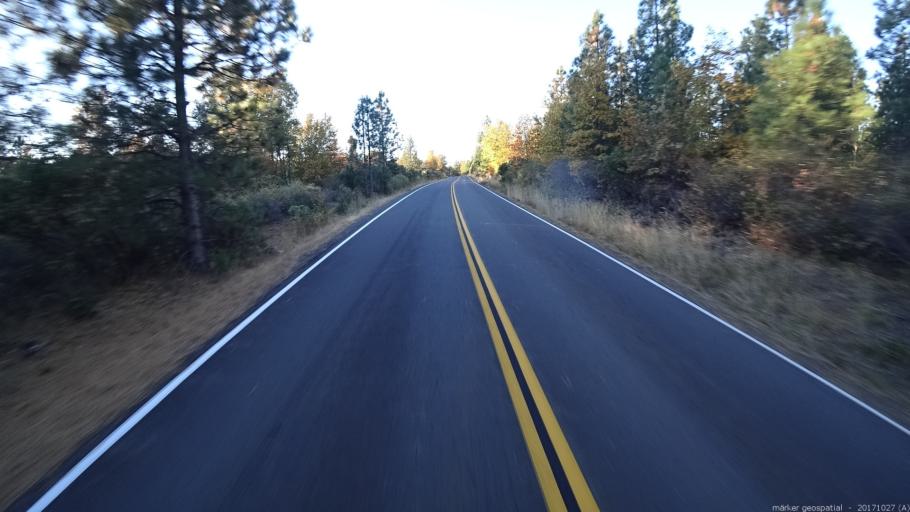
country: US
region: California
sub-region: Shasta County
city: Burney
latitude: 40.8806
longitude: -121.9081
